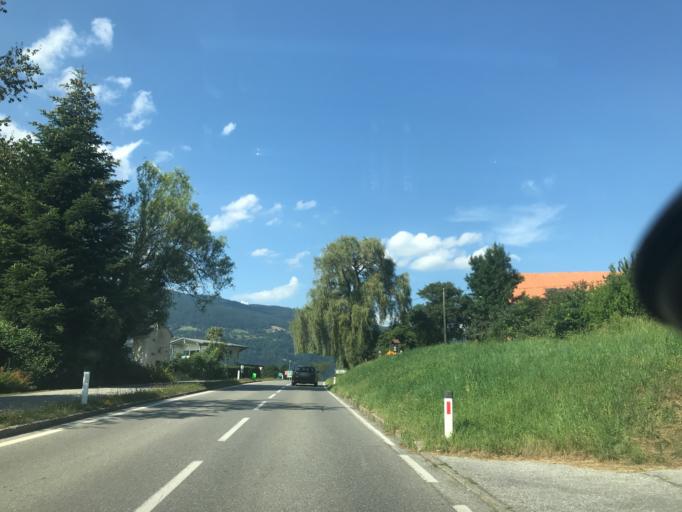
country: AT
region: Carinthia
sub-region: Politischer Bezirk Feldkirchen
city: Ossiach
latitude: 46.6669
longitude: 13.9781
